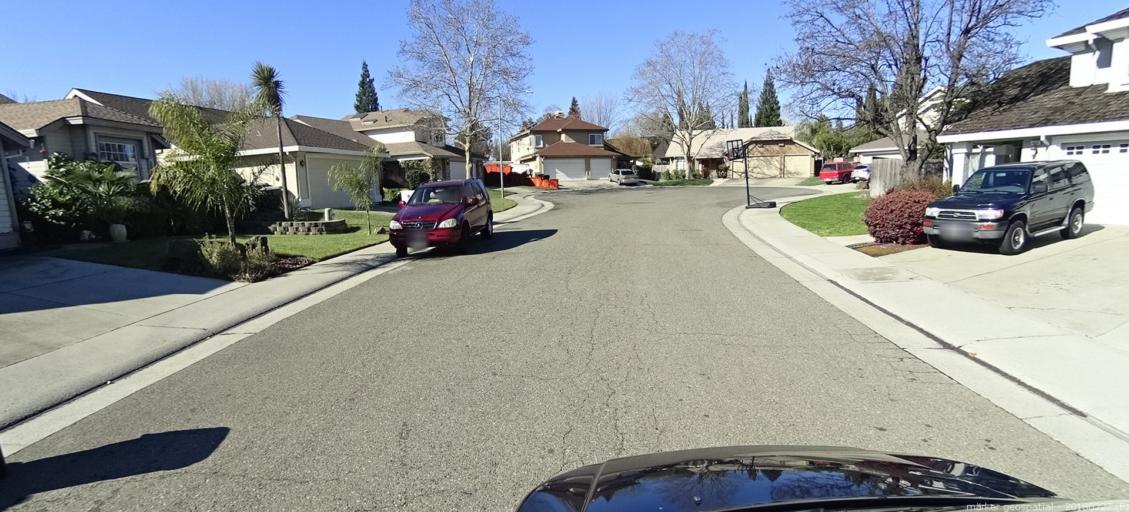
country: US
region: California
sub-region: Sacramento County
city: North Highlands
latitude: 38.7240
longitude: -121.3697
